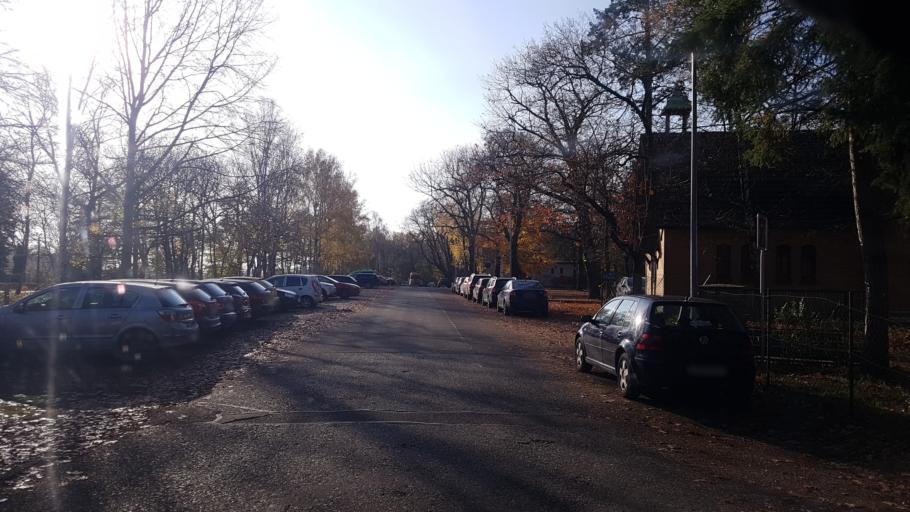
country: DE
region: Brandenburg
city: Schipkau
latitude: 51.5550
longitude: 13.8891
